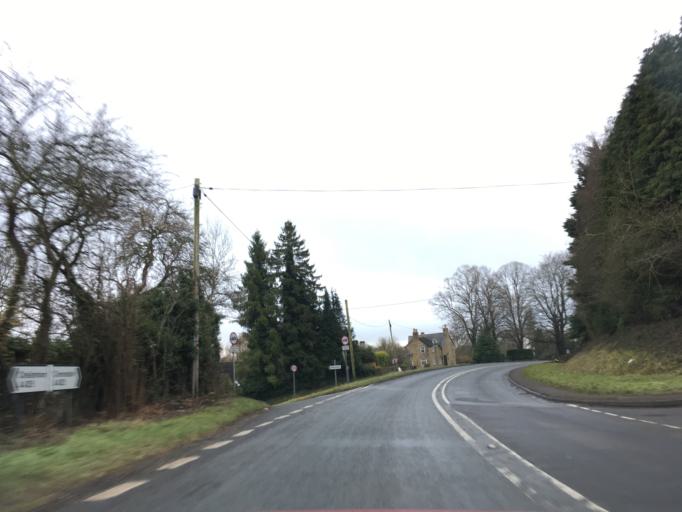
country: GB
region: England
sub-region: Gloucestershire
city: Cirencester
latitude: 51.7385
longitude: -1.9700
